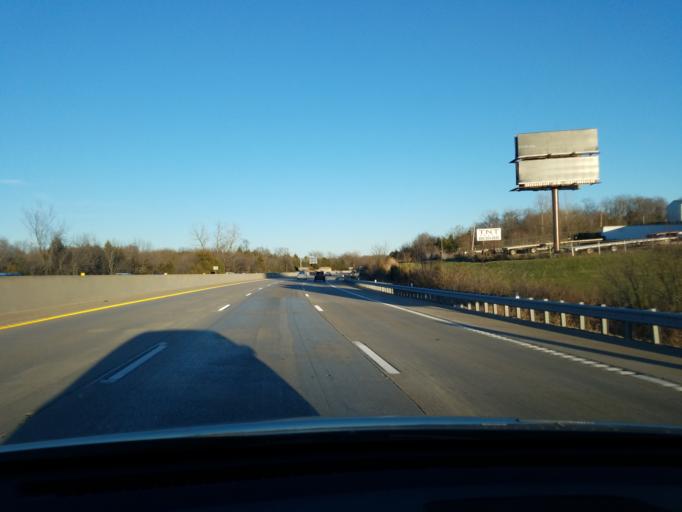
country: US
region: Missouri
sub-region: Franklin County
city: Gray Summit
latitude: 38.4823
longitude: -90.8431
